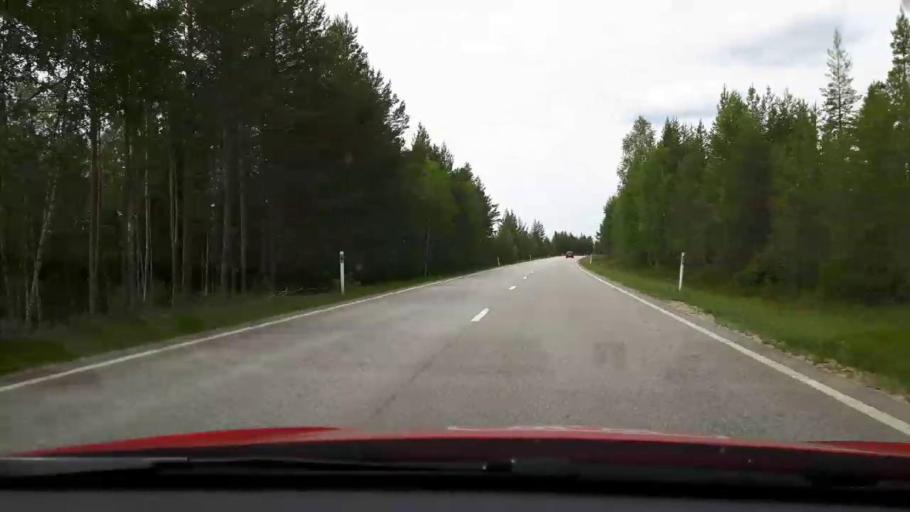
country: SE
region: Jaemtland
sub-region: Harjedalens Kommun
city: Sveg
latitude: 62.0502
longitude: 14.3157
